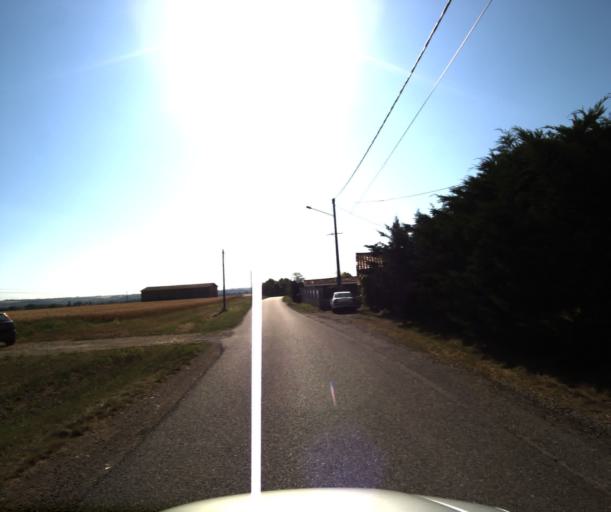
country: FR
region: Midi-Pyrenees
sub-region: Departement de la Haute-Garonne
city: Eaunes
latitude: 43.4342
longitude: 1.3721
